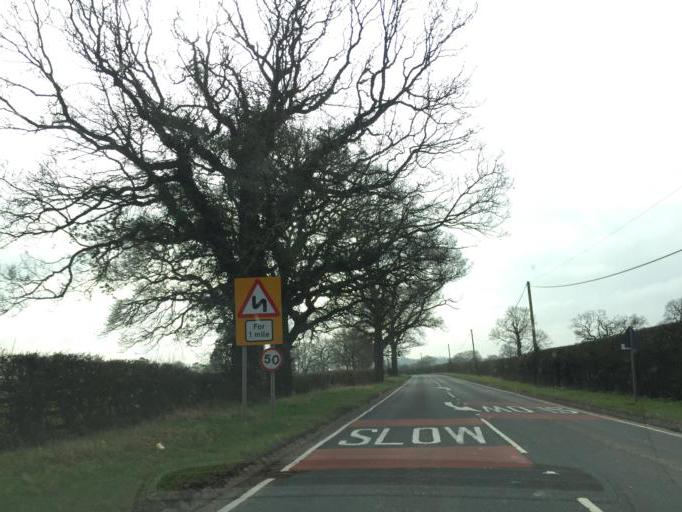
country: GB
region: England
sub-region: Warwickshire
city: Henley in Arden
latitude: 52.2963
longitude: -1.8277
